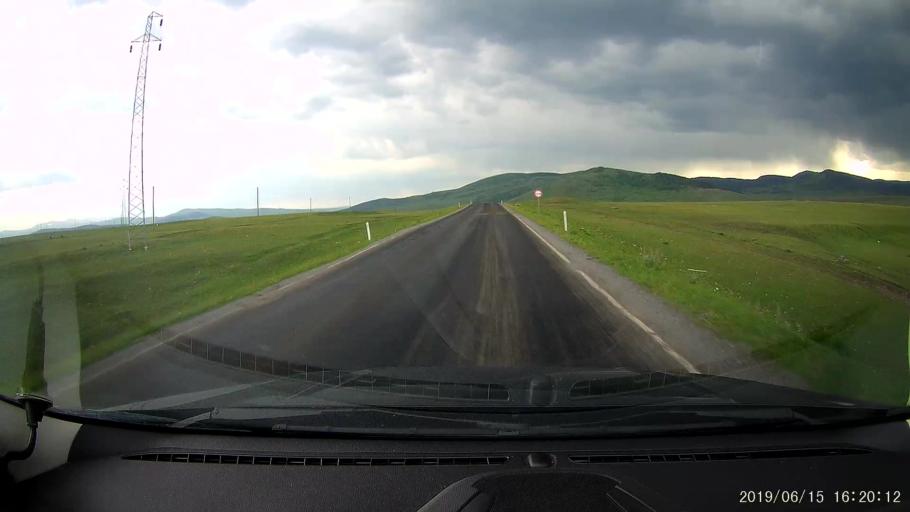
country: TR
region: Ardahan
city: Hanak
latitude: 41.2183
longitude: 42.8492
